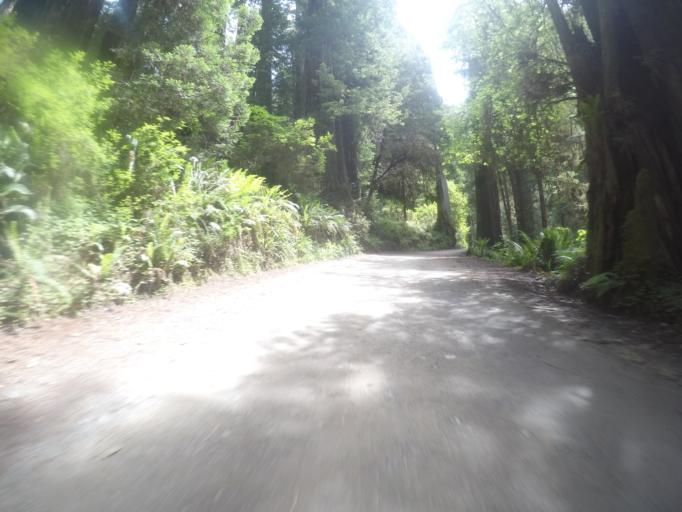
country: US
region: California
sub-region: Del Norte County
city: Bertsch-Oceanview
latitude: 41.7663
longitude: -124.1178
